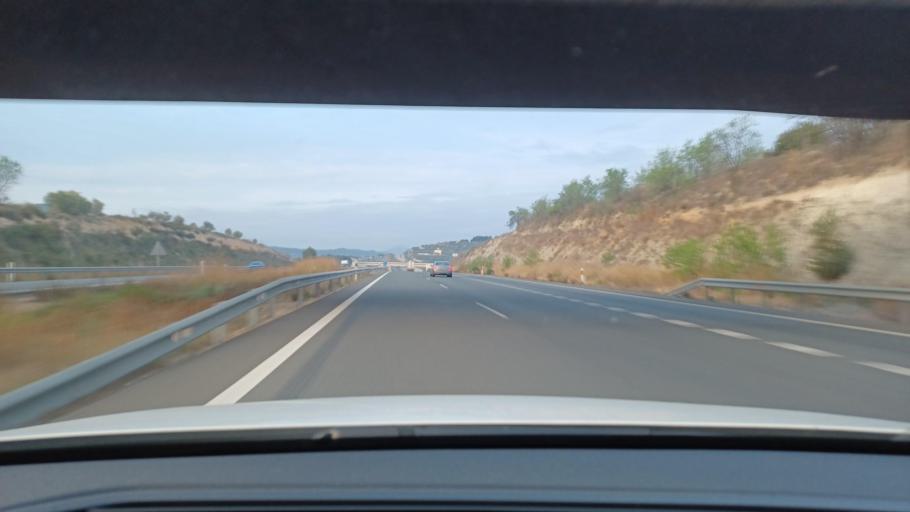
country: ES
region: Valencia
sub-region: Provincia de Valencia
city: Mogente
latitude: 38.8886
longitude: -0.7351
